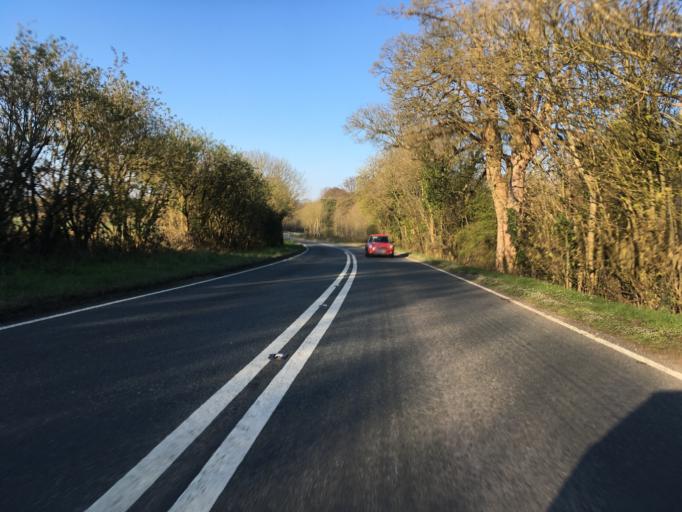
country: GB
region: England
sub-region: Oxfordshire
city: Burford
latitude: 51.8090
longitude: -1.6852
